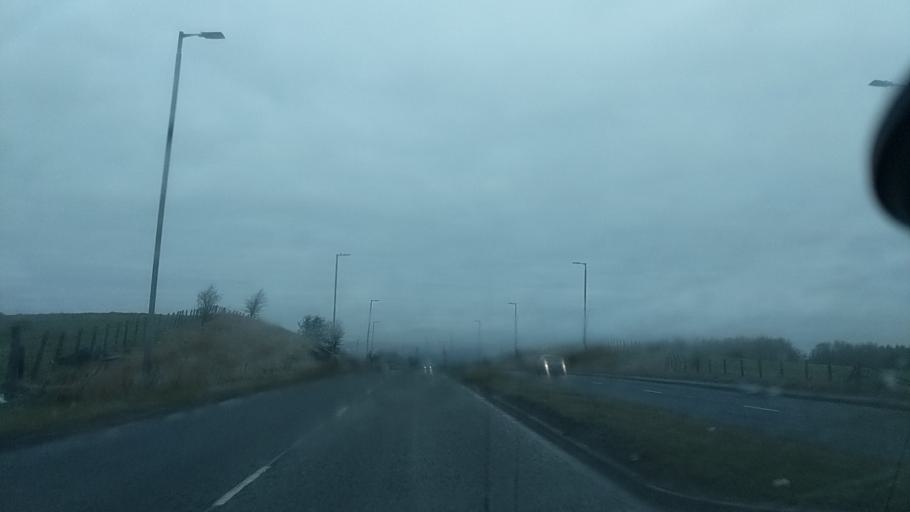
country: GB
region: Scotland
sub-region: South Lanarkshire
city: East Kilbride
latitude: 55.7950
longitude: -4.1681
